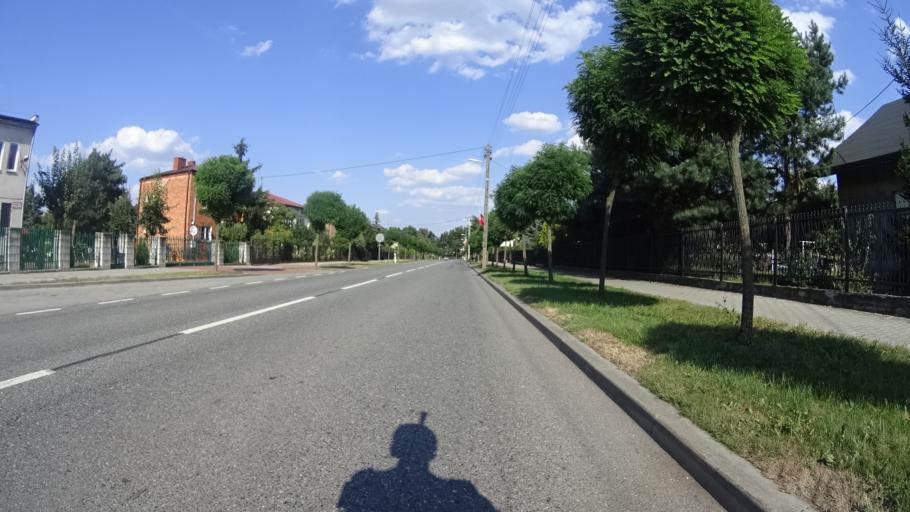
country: PL
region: Masovian Voivodeship
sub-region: Powiat bialobrzeski
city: Wysmierzyce
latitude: 51.6252
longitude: 20.8236
